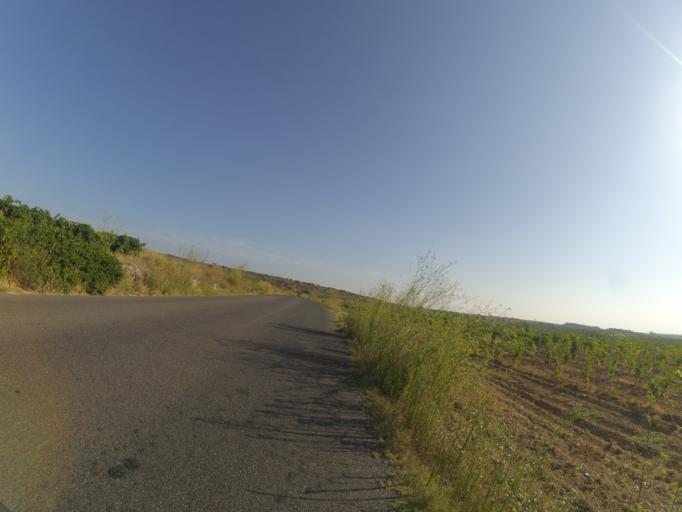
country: FR
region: Languedoc-Roussillon
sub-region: Departement des Pyrenees-Orientales
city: Baixas
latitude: 42.7594
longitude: 2.8197
